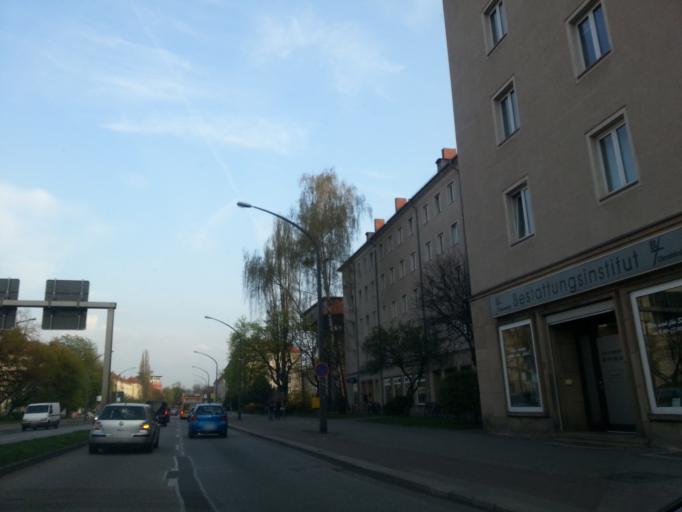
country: DE
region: Saxony
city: Dresden
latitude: 51.0366
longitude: 13.7163
